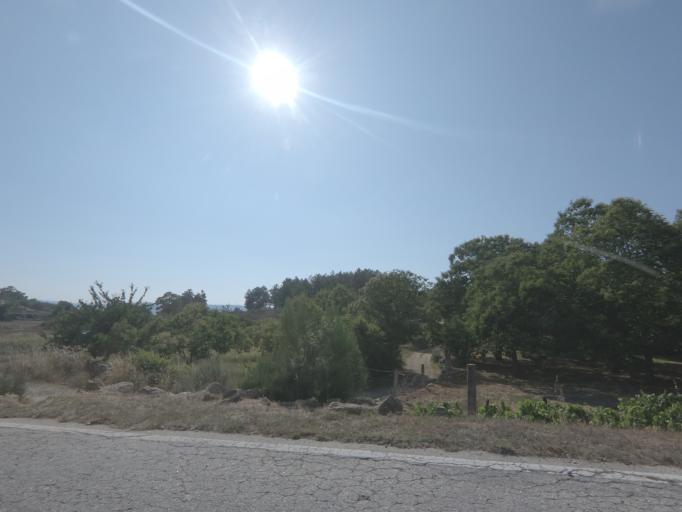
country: PT
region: Viseu
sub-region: Tabuaco
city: Tabuaco
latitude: 41.0554
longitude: -7.5657
